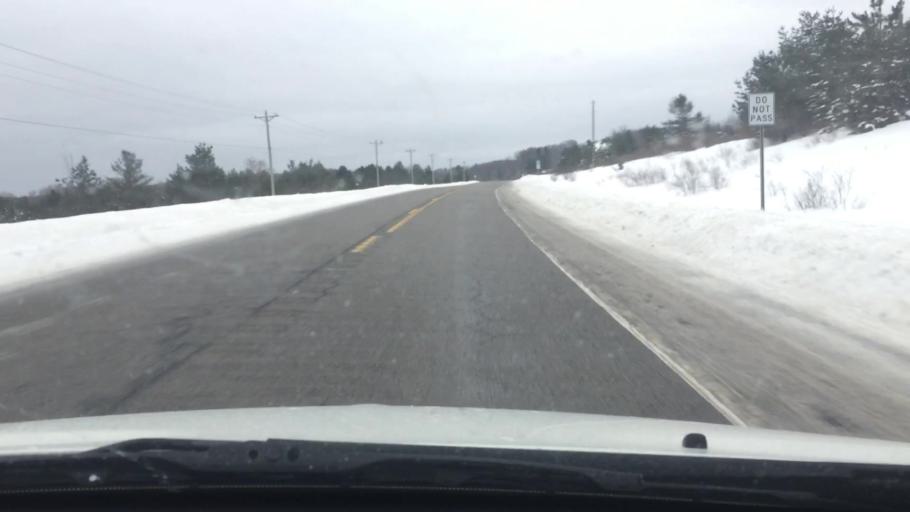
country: US
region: Michigan
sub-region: Charlevoix County
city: East Jordan
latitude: 45.1180
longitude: -85.1295
